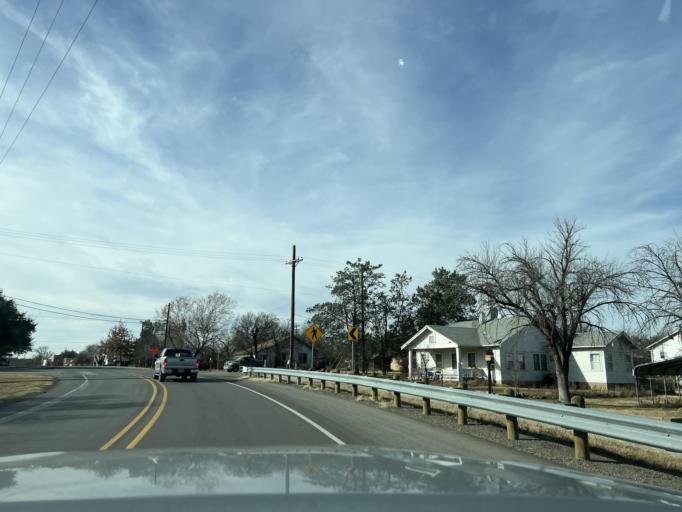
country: US
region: Texas
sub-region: Shackelford County
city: Albany
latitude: 32.7233
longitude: -99.2934
